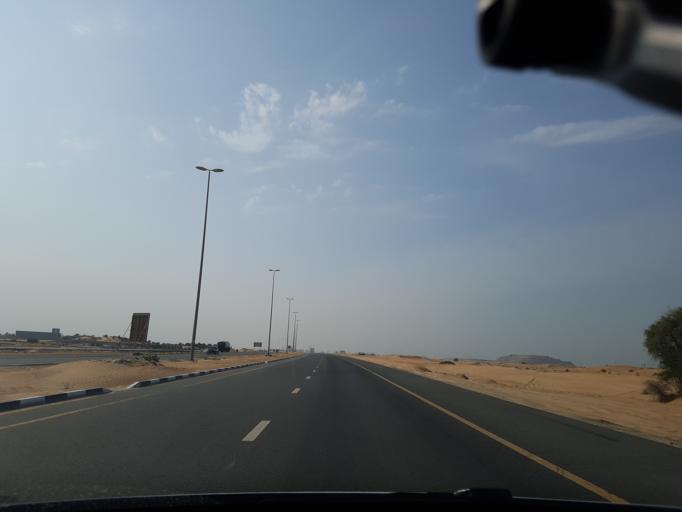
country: AE
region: Ajman
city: Ajman
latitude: 25.4087
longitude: 55.5715
